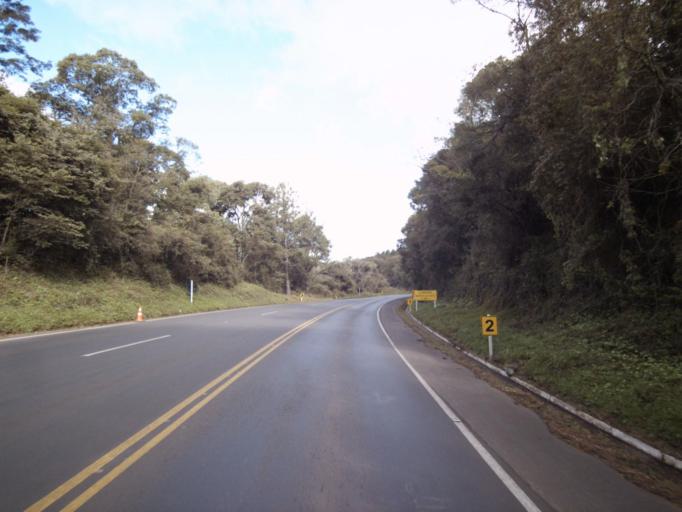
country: BR
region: Santa Catarina
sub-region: Joacaba
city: Joacaba
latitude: -26.9874
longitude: -51.7532
